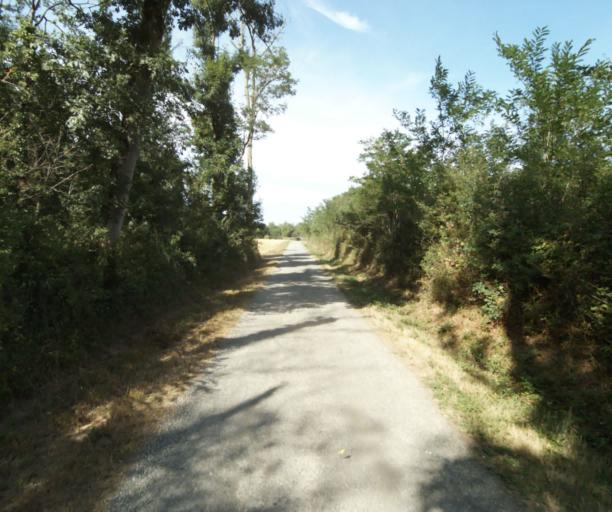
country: FR
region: Midi-Pyrenees
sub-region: Departement du Tarn
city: Soual
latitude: 43.5162
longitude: 2.0903
